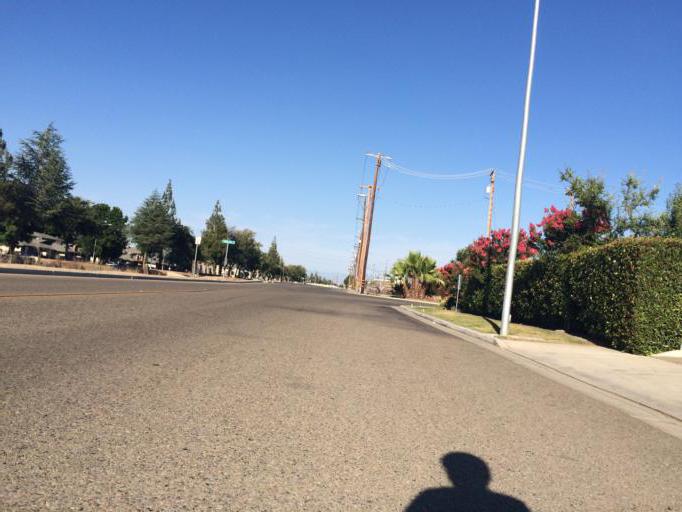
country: US
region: California
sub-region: Fresno County
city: Fresno
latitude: 36.7648
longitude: -119.7415
